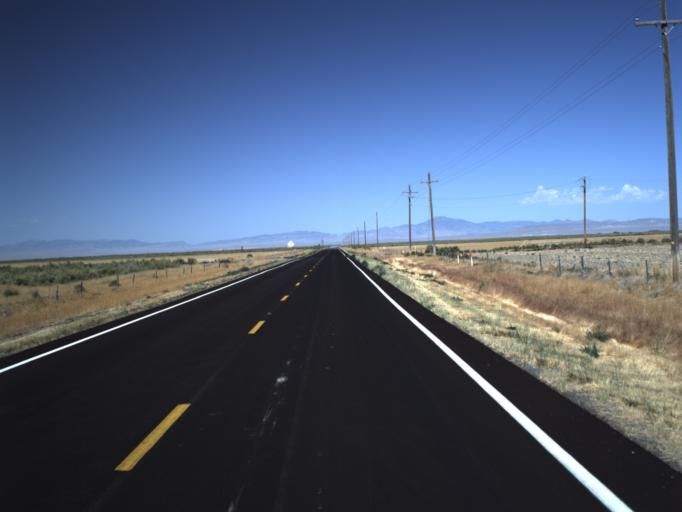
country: US
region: Utah
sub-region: Millard County
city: Delta
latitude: 39.3309
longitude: -112.6926
